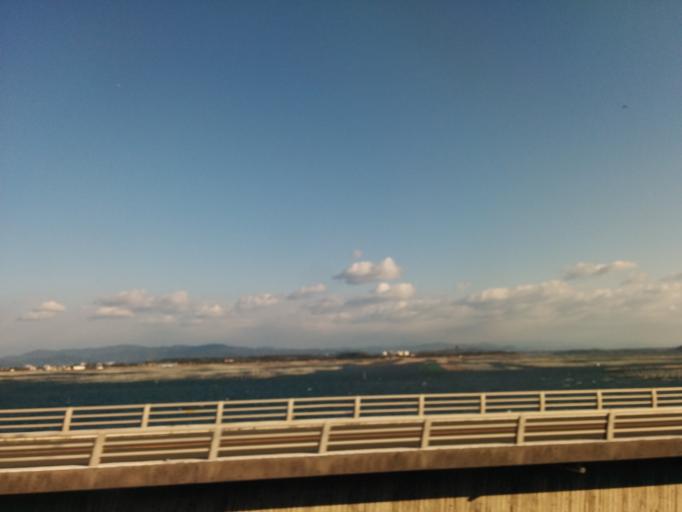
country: JP
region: Shizuoka
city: Kosai-shi
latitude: 34.6948
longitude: 137.5890
